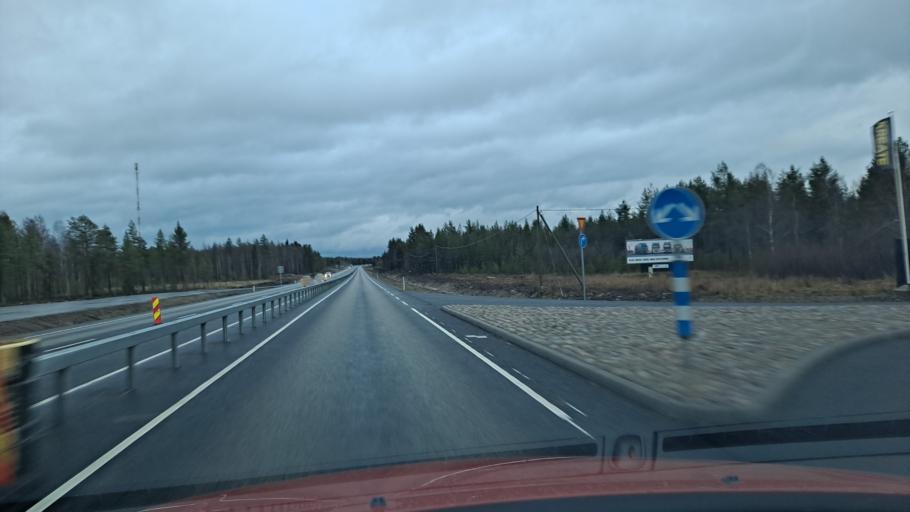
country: FI
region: Northern Ostrobothnia
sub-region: Oulunkaari
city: Kuivaniemi
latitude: 65.6271
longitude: 25.1362
